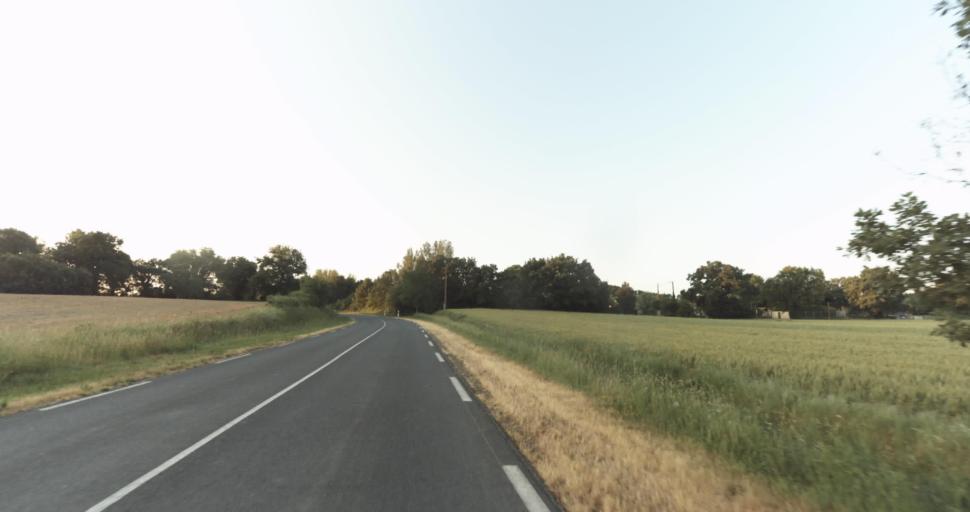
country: FR
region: Midi-Pyrenees
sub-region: Departement du Gers
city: Pujaudran
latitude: 43.6392
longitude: 1.1442
